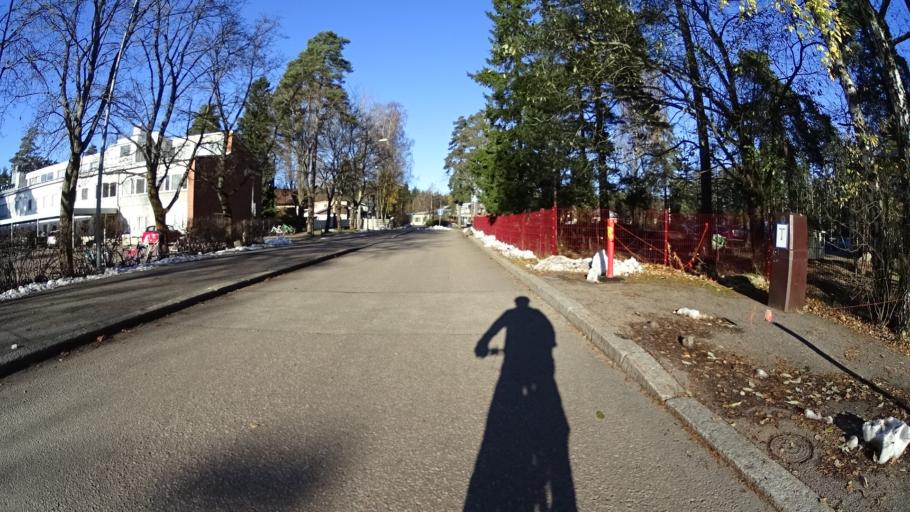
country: FI
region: Uusimaa
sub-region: Helsinki
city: Kauniainen
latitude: 60.2133
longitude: 24.7165
